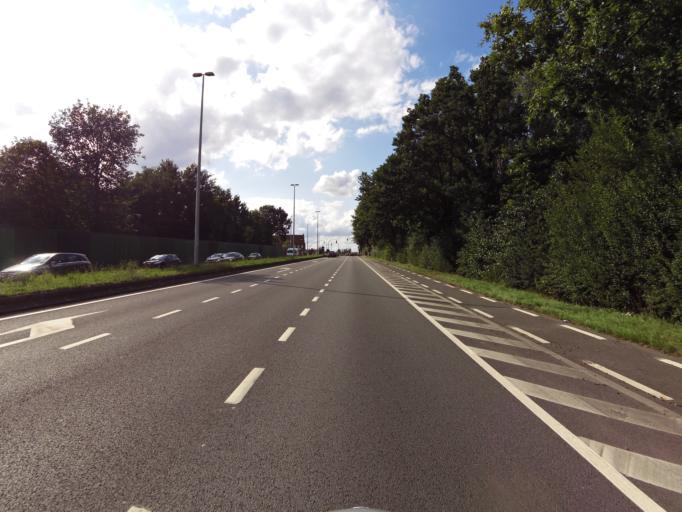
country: BE
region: Flanders
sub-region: Provincie West-Vlaanderen
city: Waregem
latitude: 50.8778
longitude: 3.4259
